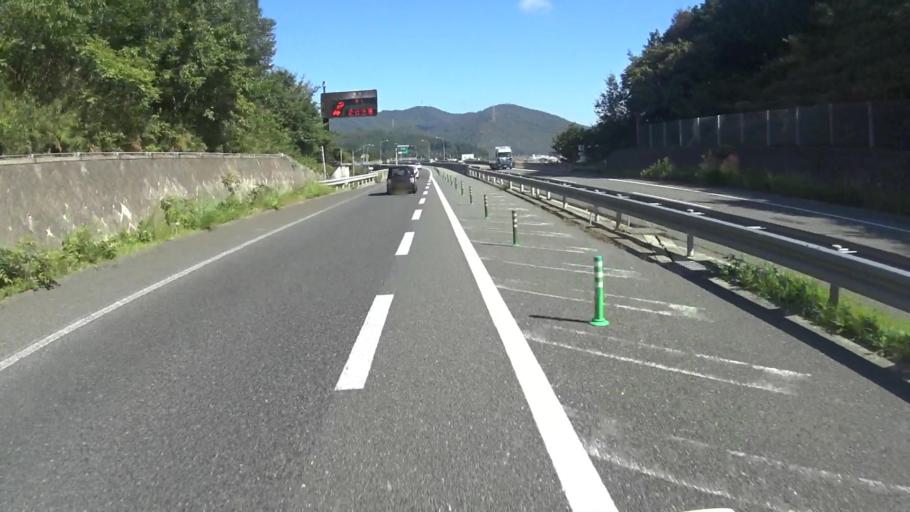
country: JP
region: Kyoto
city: Kameoka
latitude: 35.1175
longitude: 135.4799
